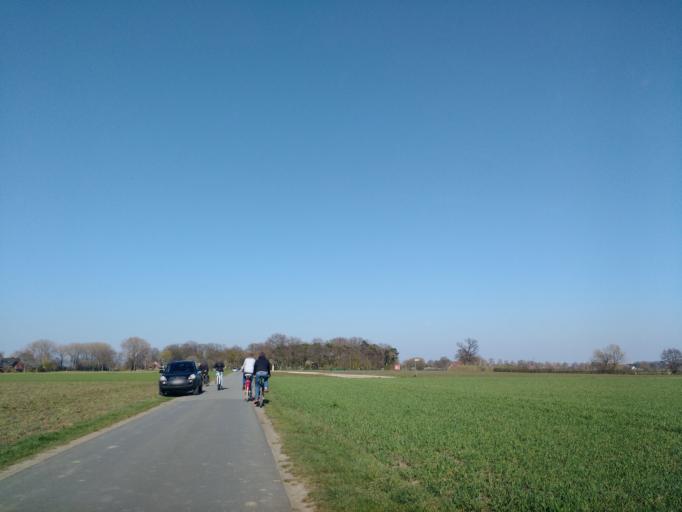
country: DE
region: North Rhine-Westphalia
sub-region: Regierungsbezirk Detmold
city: Delbruck
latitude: 51.7366
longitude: 8.5897
